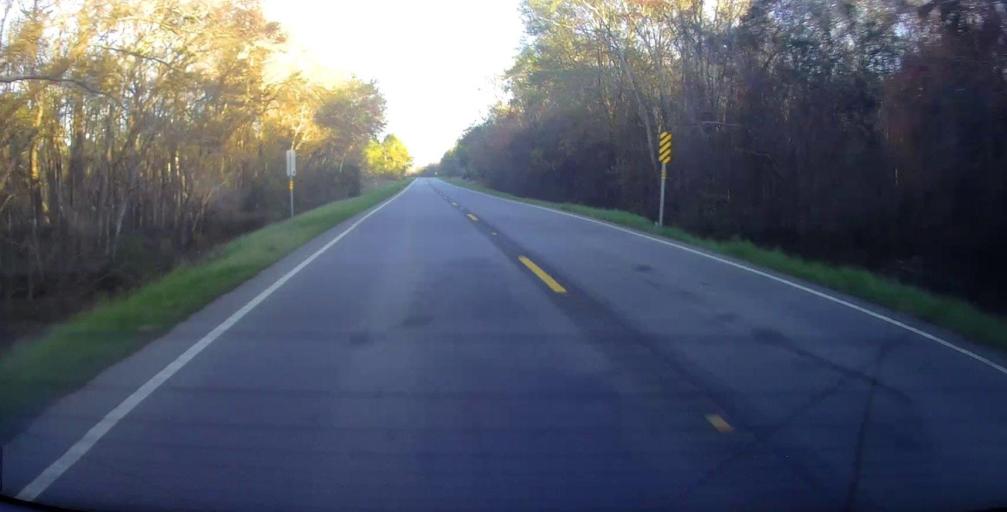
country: US
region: Georgia
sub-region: Wilcox County
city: Rochelle
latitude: 31.9471
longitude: -83.5594
